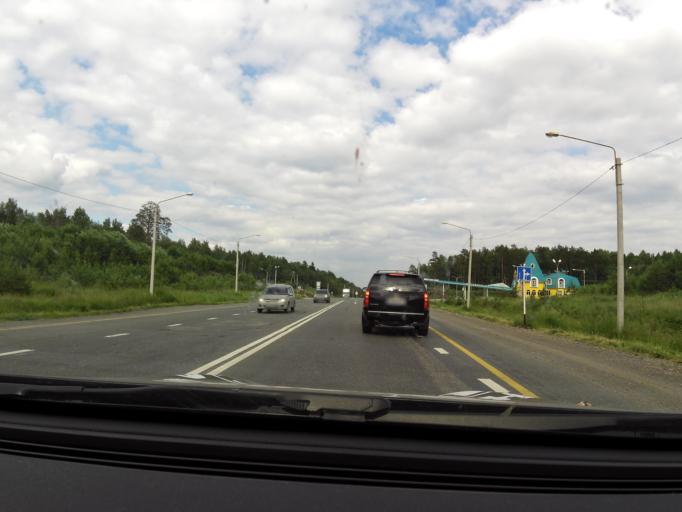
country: RU
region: Sverdlovsk
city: Druzhinino
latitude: 56.8047
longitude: 59.4821
